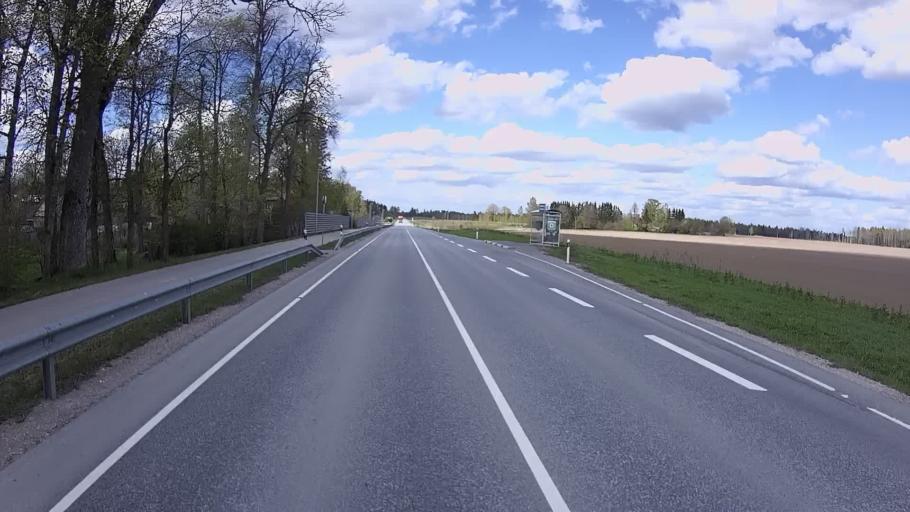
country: EE
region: Jogevamaa
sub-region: Jogeva linn
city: Jogeva
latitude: 58.7610
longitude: 26.3340
